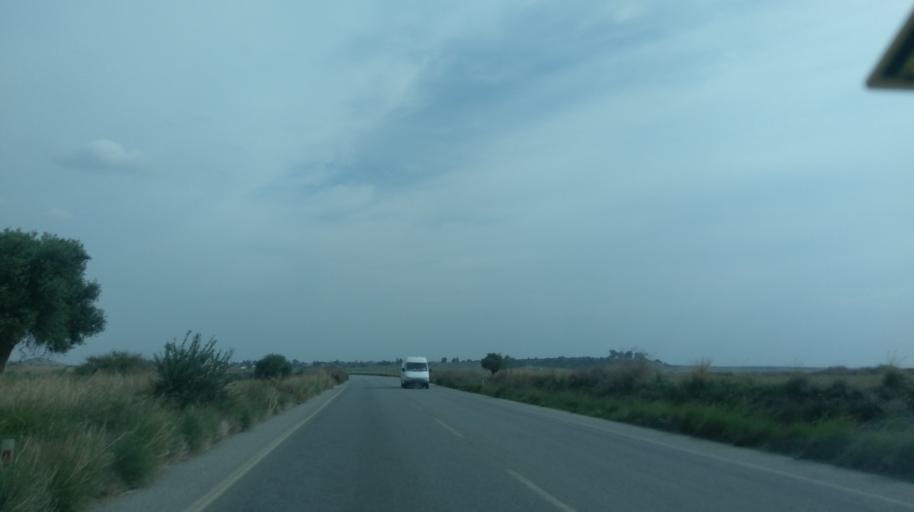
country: CY
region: Ammochostos
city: Lefkonoiko
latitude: 35.2615
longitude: 33.7590
